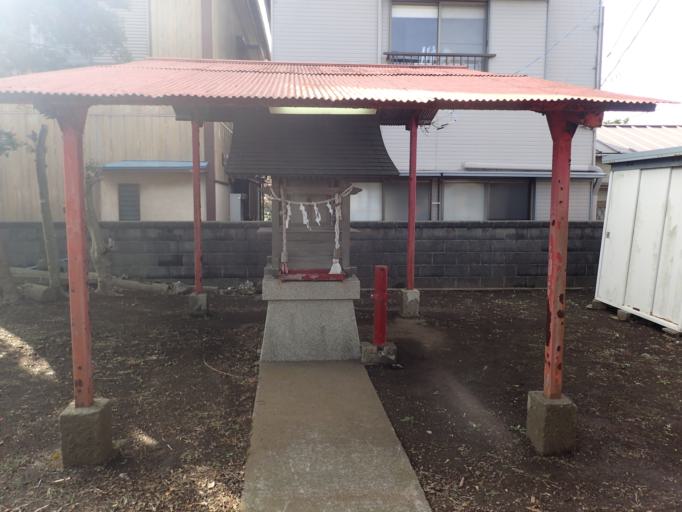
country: JP
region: Kanagawa
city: Miura
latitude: 35.1414
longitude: 139.6266
